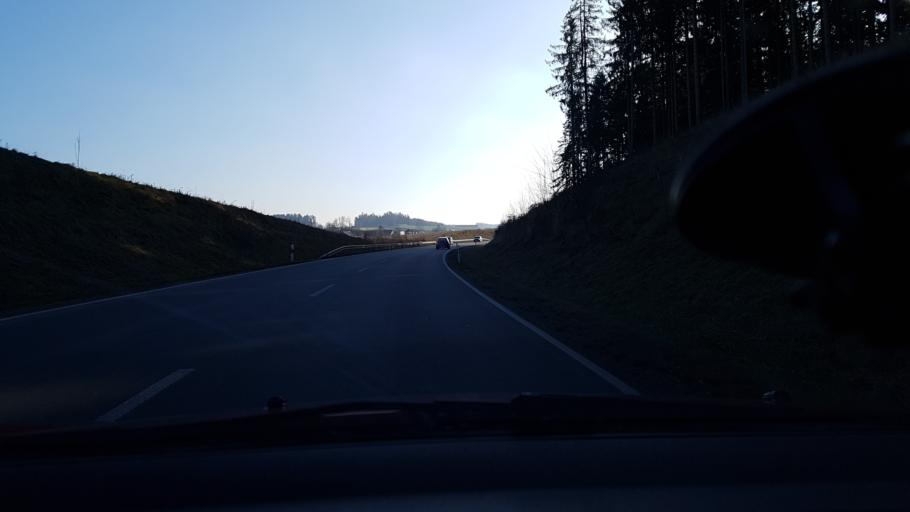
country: DE
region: Bavaria
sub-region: Lower Bavaria
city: Pfarrkirchen
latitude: 48.3808
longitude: 12.9534
